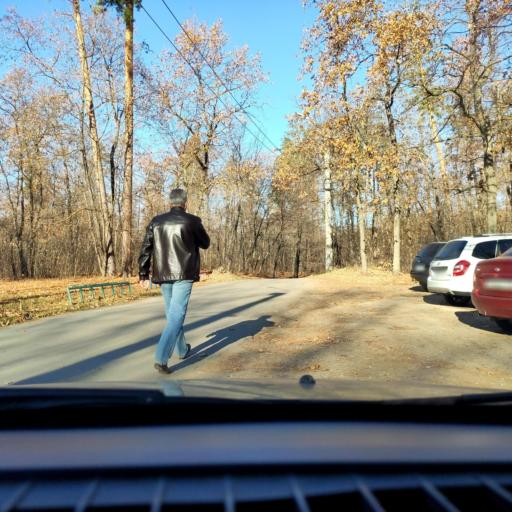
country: RU
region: Samara
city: Tol'yatti
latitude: 53.4913
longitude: 49.3015
